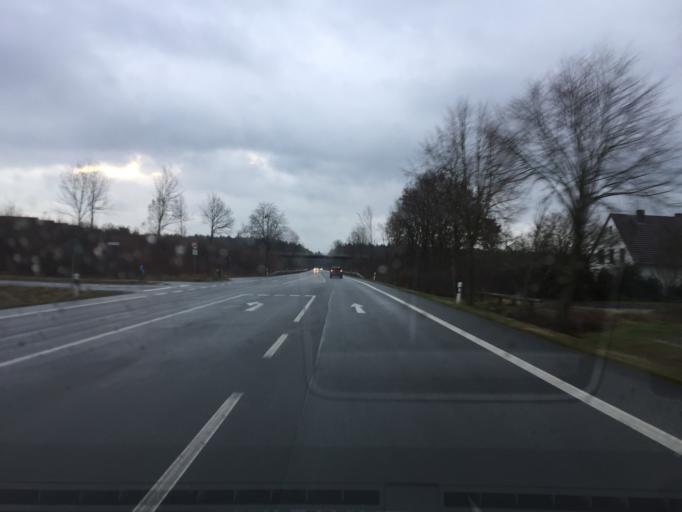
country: DE
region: North Rhine-Westphalia
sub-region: Regierungsbezirk Detmold
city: Petershagen
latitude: 52.3717
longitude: 8.9551
